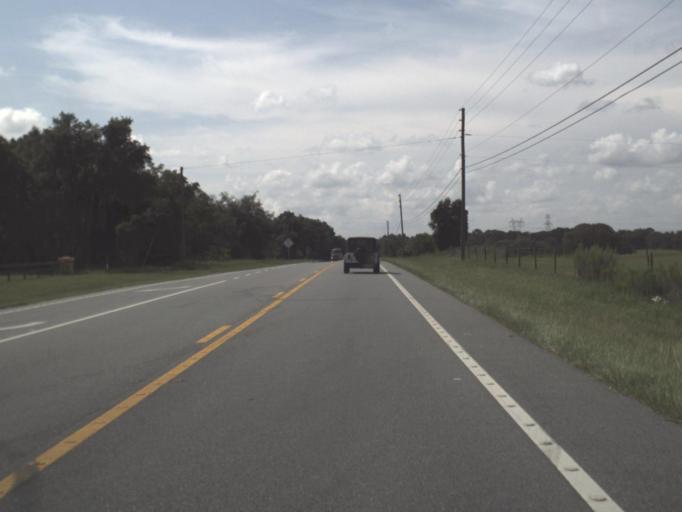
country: US
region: Florida
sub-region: Citrus County
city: Beverly Hills
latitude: 28.9541
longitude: -82.4110
